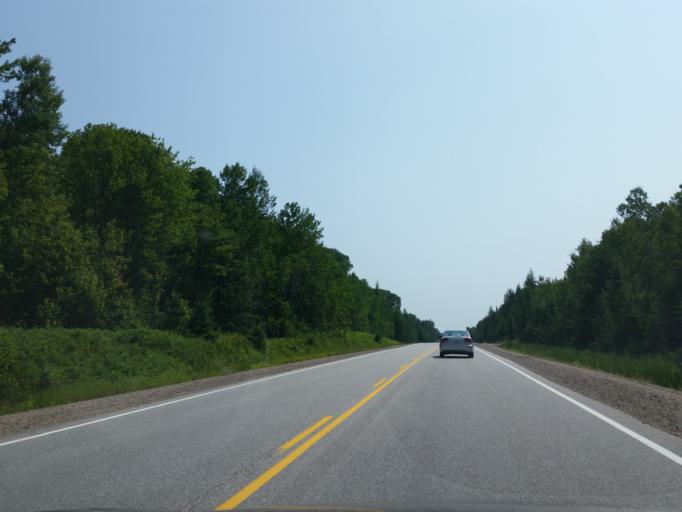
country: CA
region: Ontario
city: Mattawa
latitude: 46.2770
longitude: -78.4547
